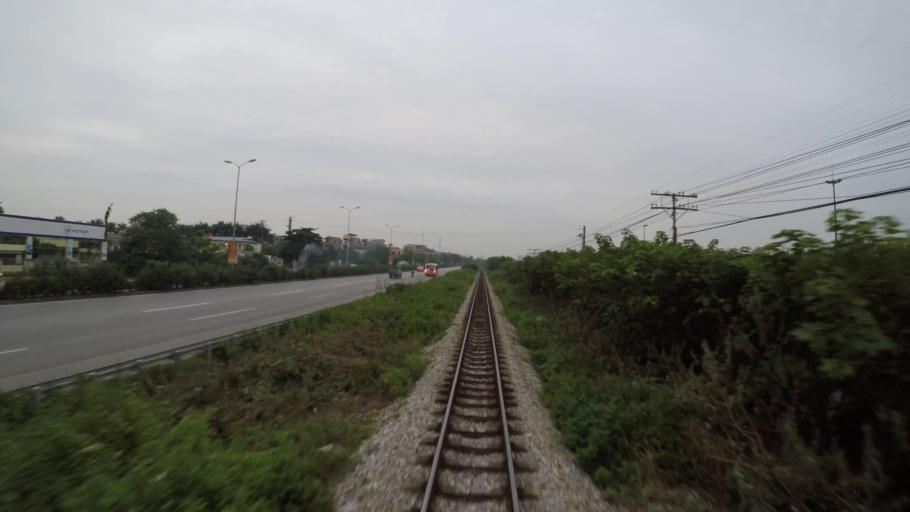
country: VN
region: Ha Noi
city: Trau Quy
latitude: 21.0132
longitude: 105.9490
